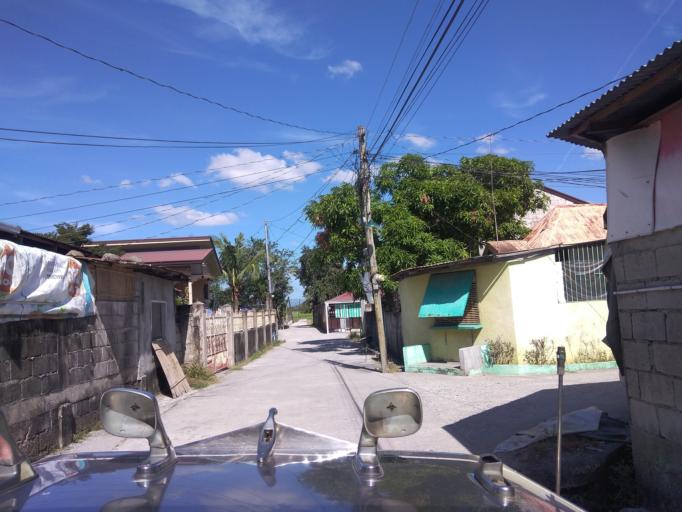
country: PH
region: Central Luzon
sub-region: Province of Pampanga
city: San Agustin
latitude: 14.9923
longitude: 120.6071
